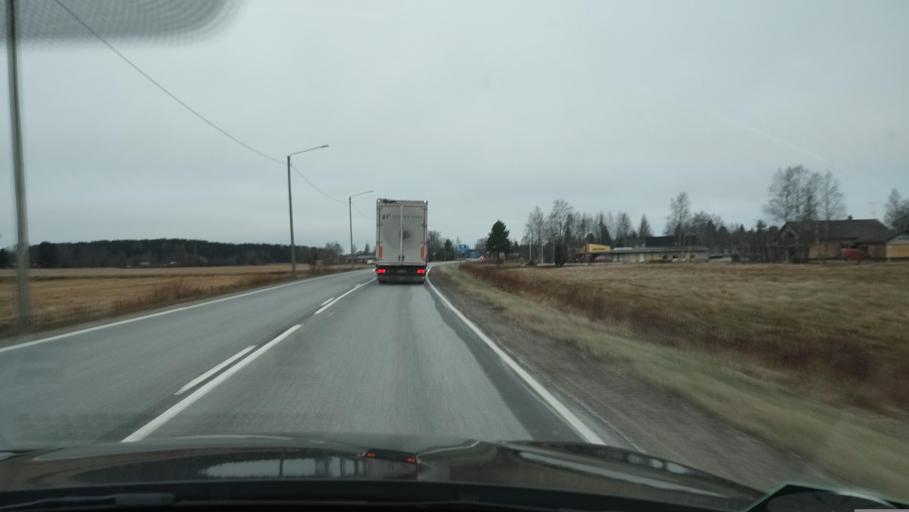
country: FI
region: Southern Ostrobothnia
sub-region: Suupohja
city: Kauhajoki
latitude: 62.3578
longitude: 22.0670
